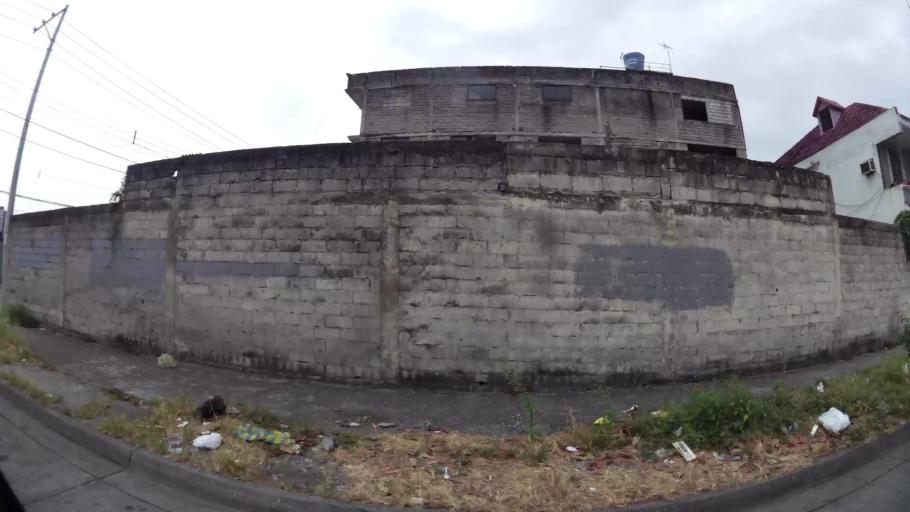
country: EC
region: Guayas
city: Eloy Alfaro
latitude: -2.1482
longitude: -79.8874
